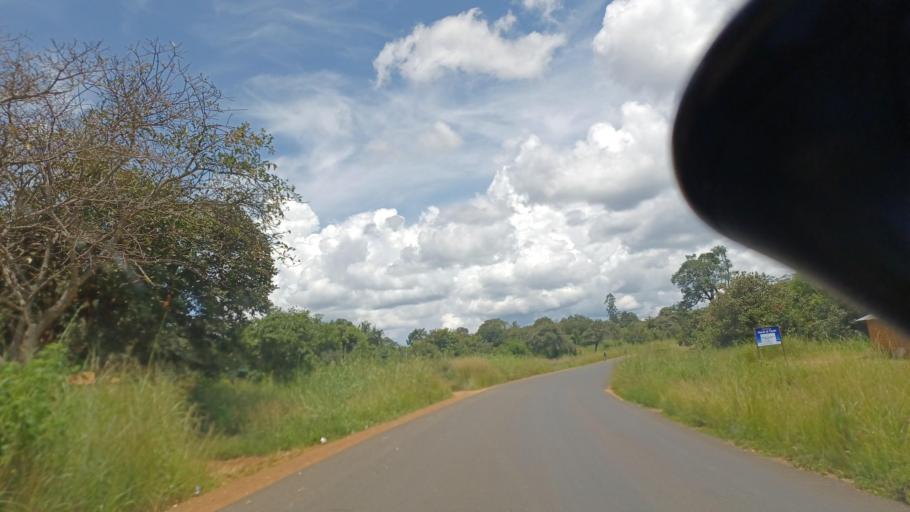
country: ZM
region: North-Western
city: Solwezi
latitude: -12.4050
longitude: 26.2402
